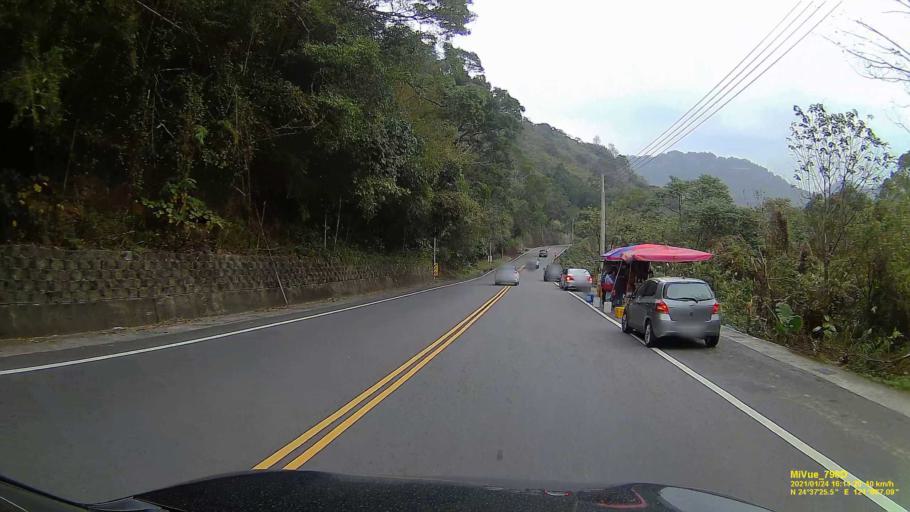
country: TW
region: Taiwan
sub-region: Hsinchu
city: Hsinchu
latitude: 24.6240
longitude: 121.0021
